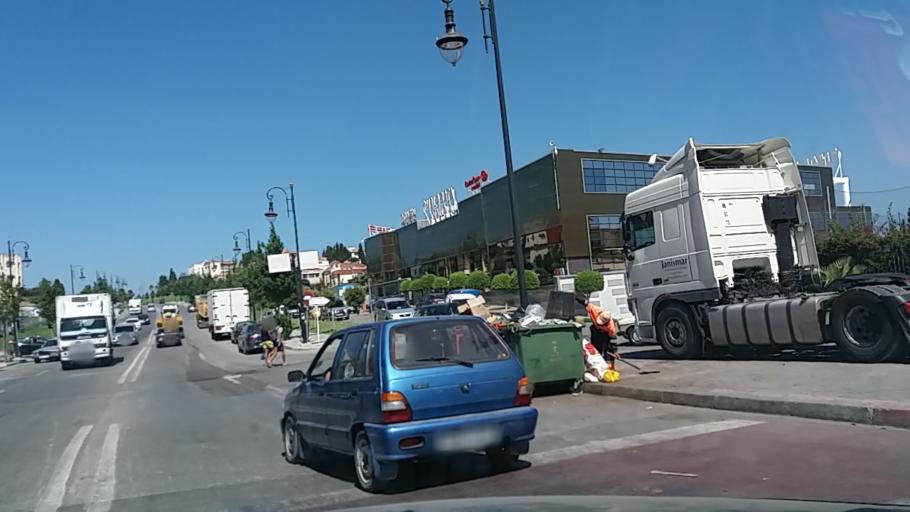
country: MA
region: Tanger-Tetouan
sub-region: Tanger-Assilah
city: Tangier
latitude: 35.7719
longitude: -5.7697
